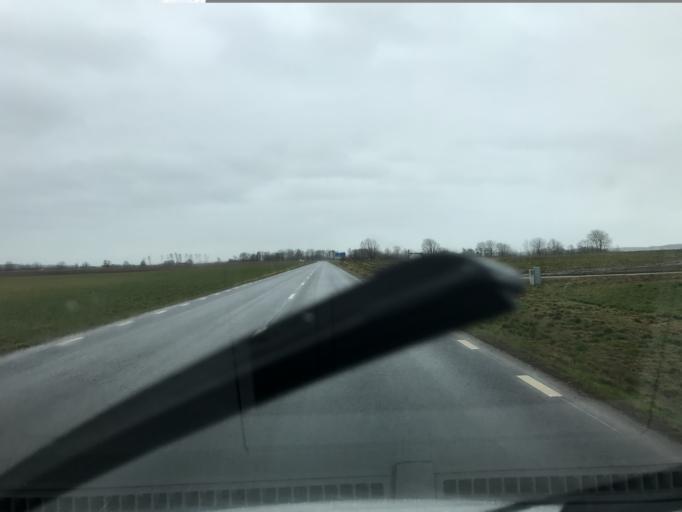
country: SE
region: Skane
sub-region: Bastads Kommun
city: Forslov
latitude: 56.3259
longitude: 12.8878
